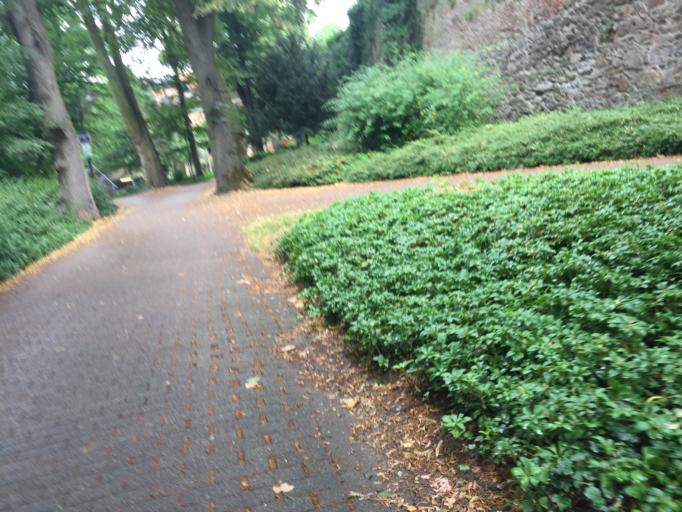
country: DE
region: Baden-Wuerttemberg
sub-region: Freiburg Region
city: Offenburg
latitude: 48.4708
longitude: 7.9403
